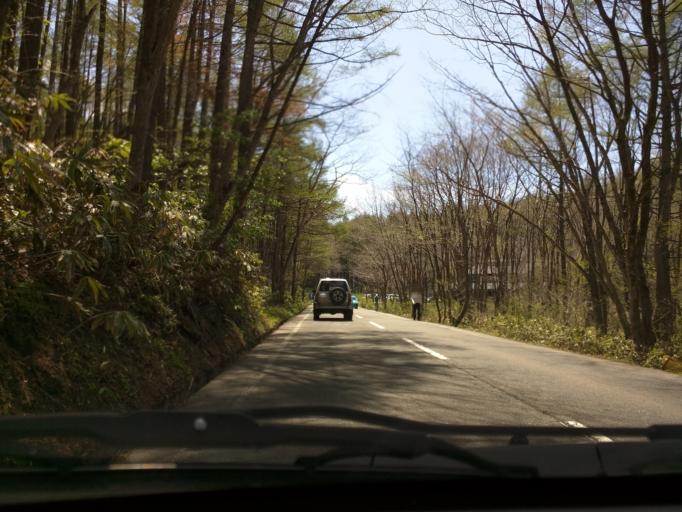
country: JP
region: Nagano
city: Nagano-shi
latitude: 36.7484
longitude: 138.0775
